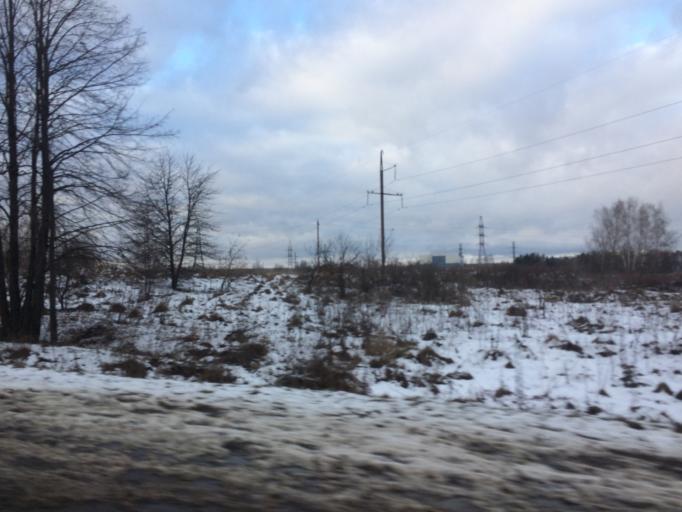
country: RU
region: Tula
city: Ageyevo
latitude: 54.1313
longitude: 36.4695
